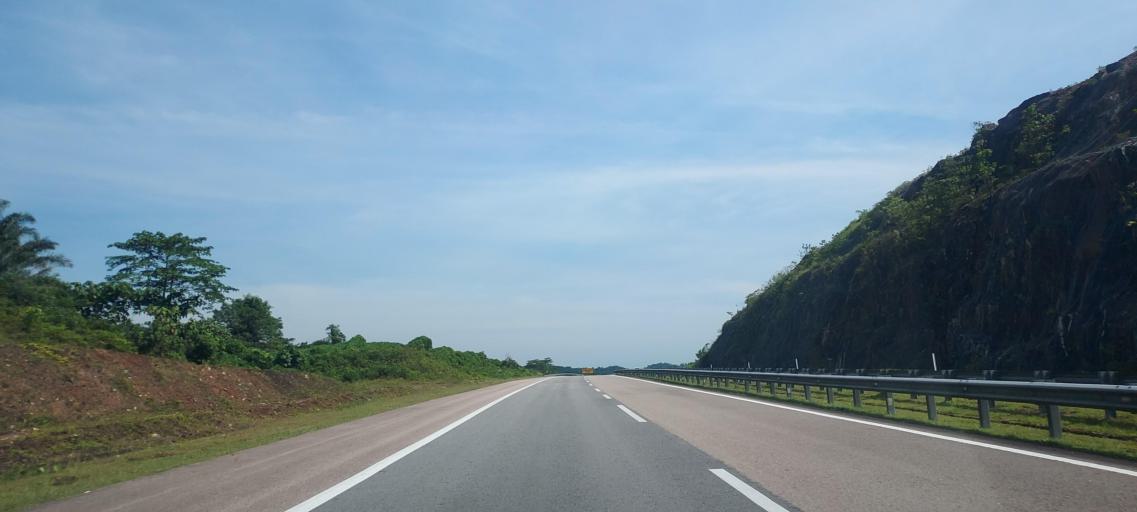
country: MY
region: Terengganu
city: Marang
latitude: 4.9515
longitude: 103.0865
